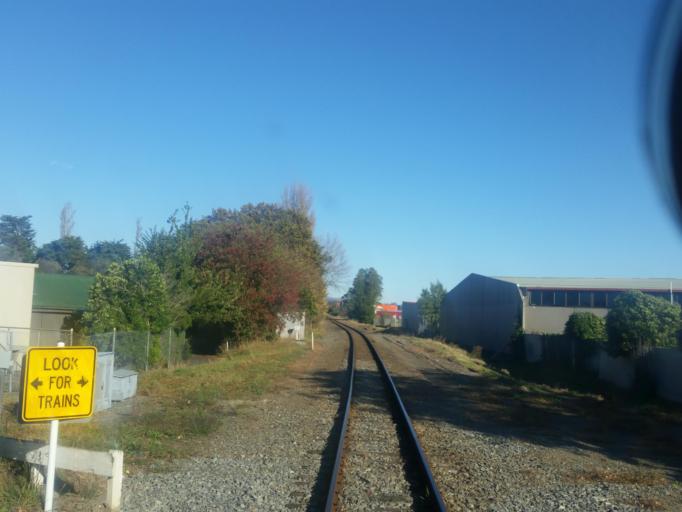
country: NZ
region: Canterbury
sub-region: Christchurch City
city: Christchurch
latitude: -43.4876
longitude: 172.6059
